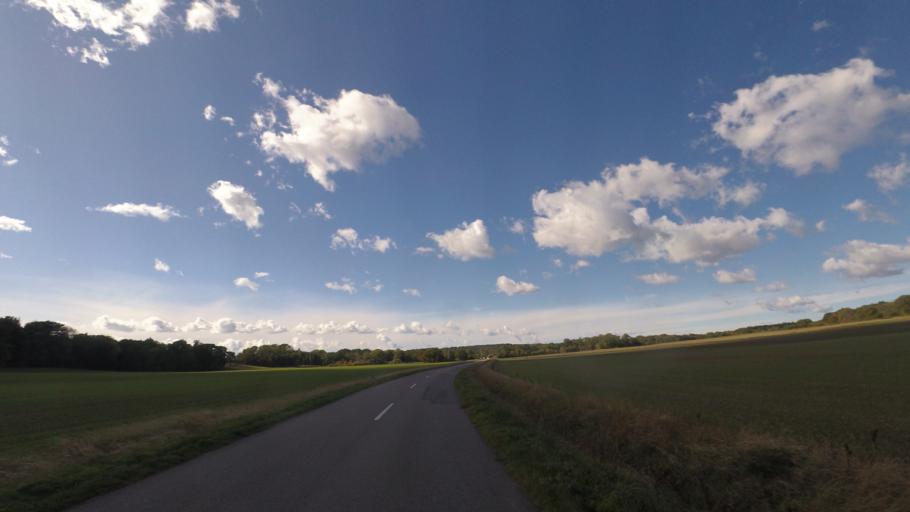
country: DK
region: Capital Region
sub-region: Bornholm Kommune
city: Nexo
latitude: 55.0774
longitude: 15.0882
